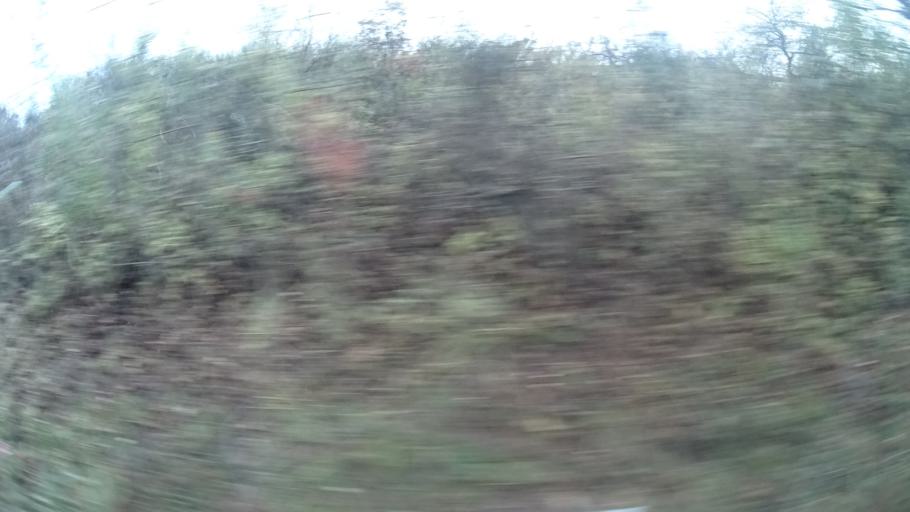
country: DE
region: Hesse
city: Heringen
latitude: 50.9045
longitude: 10.0125
